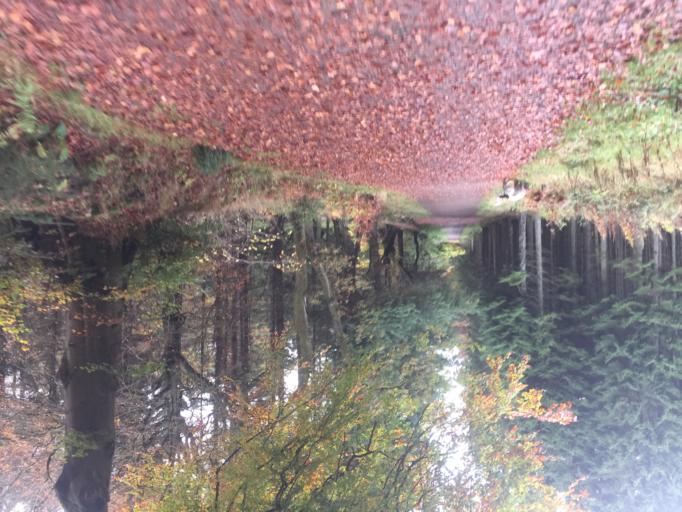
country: GB
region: Scotland
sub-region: West Lothian
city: Linlithgow
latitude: 55.9475
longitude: -3.5968
